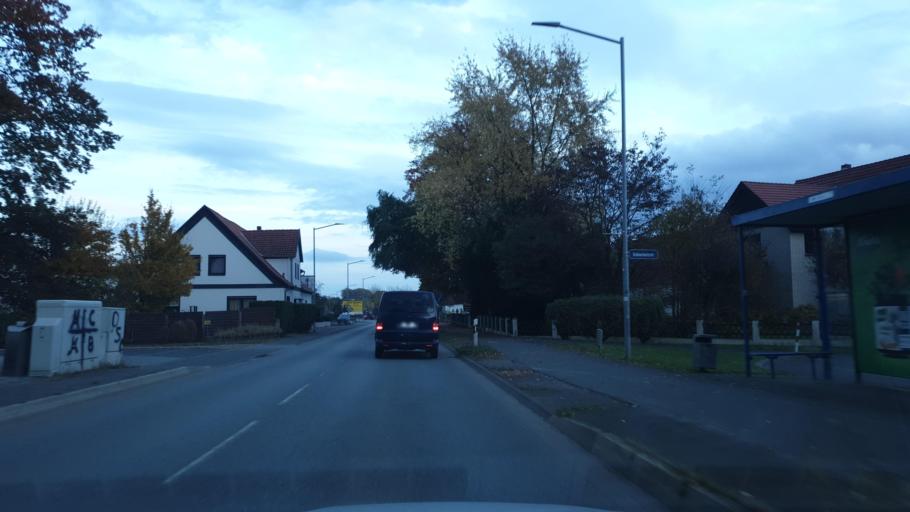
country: DE
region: North Rhine-Westphalia
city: Buende
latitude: 52.1928
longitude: 8.5293
